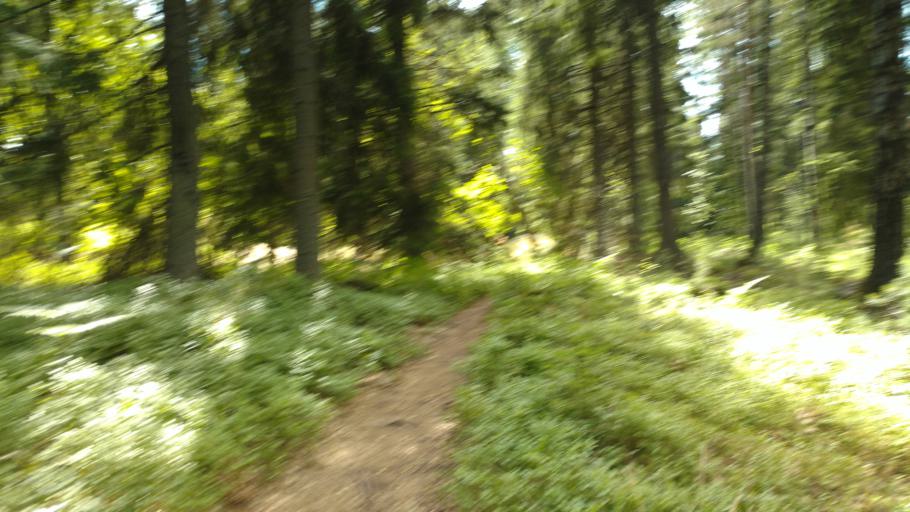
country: FI
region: Uusimaa
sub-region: Raaseporin
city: Pohja
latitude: 60.1094
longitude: 23.5512
